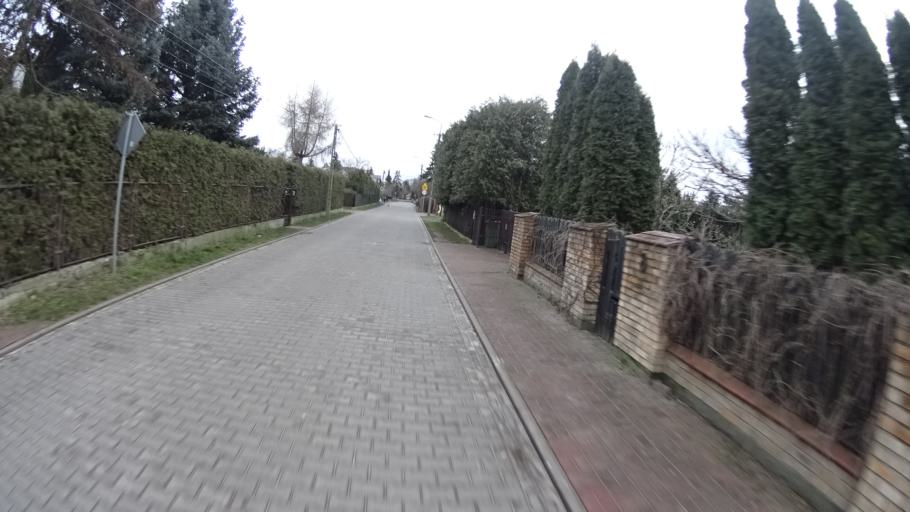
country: PL
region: Masovian Voivodeship
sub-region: Powiat pruszkowski
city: Granica
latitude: 52.1424
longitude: 20.7965
